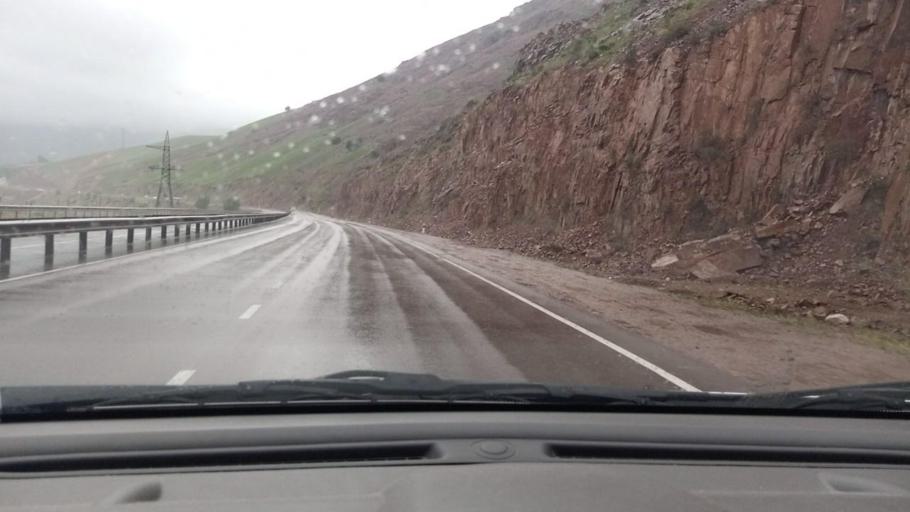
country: UZ
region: Toshkent
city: Angren
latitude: 41.1175
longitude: 70.3446
